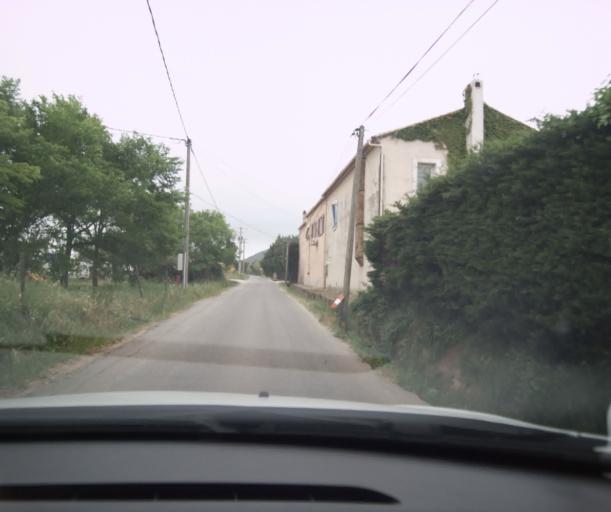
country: FR
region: Provence-Alpes-Cote d'Azur
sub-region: Departement du Var
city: Le Pradet
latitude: 43.1228
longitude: 6.0456
